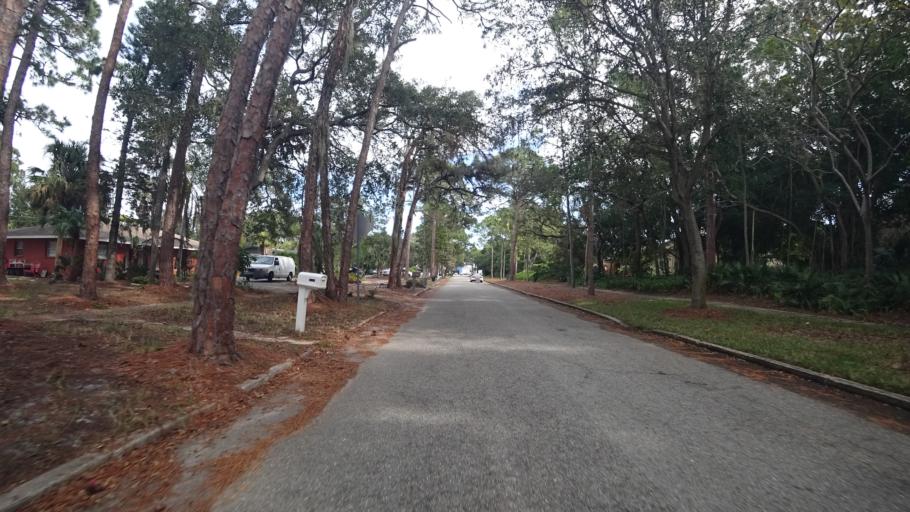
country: US
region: Florida
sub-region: Manatee County
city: West Bradenton
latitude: 27.4980
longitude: -82.6386
